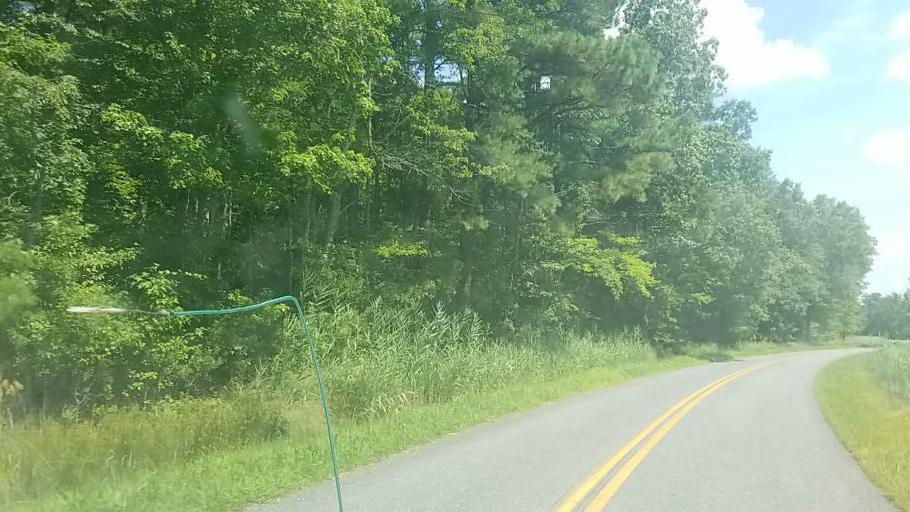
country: US
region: Maryland
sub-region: Dorchester County
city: Hurlock
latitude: 38.4320
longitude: -75.8872
